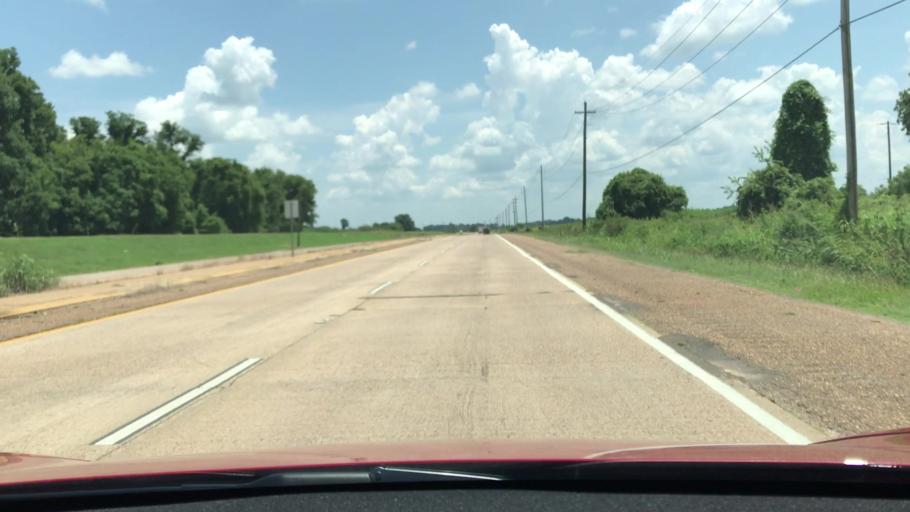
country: US
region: Louisiana
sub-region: Bossier Parish
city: Bossier City
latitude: 32.3961
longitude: -93.6891
